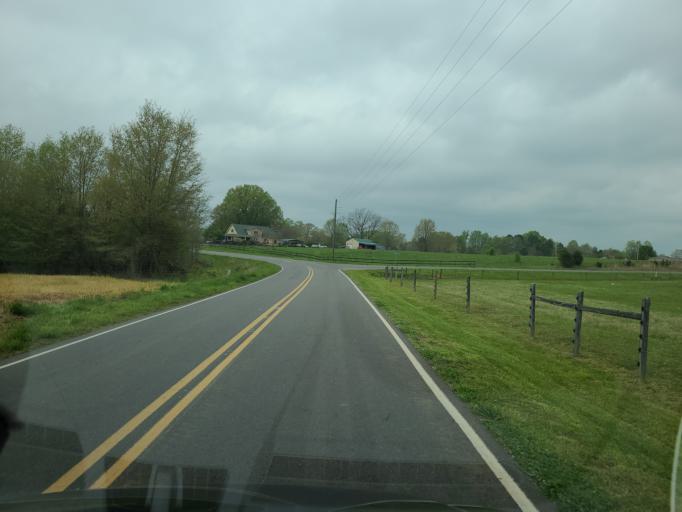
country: US
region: North Carolina
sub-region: Gaston County
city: Cherryville
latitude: 35.4378
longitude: -81.4039
